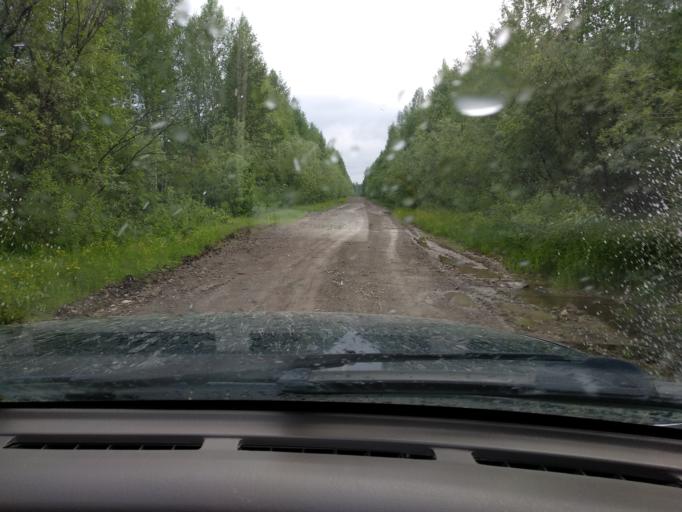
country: RU
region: Sverdlovsk
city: Karpinsk
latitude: 59.4275
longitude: 59.9643
